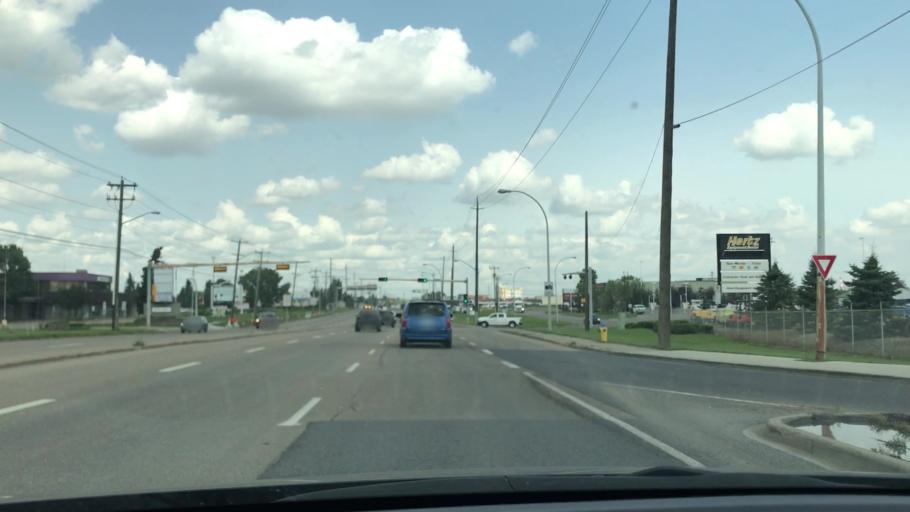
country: CA
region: Alberta
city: Edmonton
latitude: 53.5151
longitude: -113.4184
